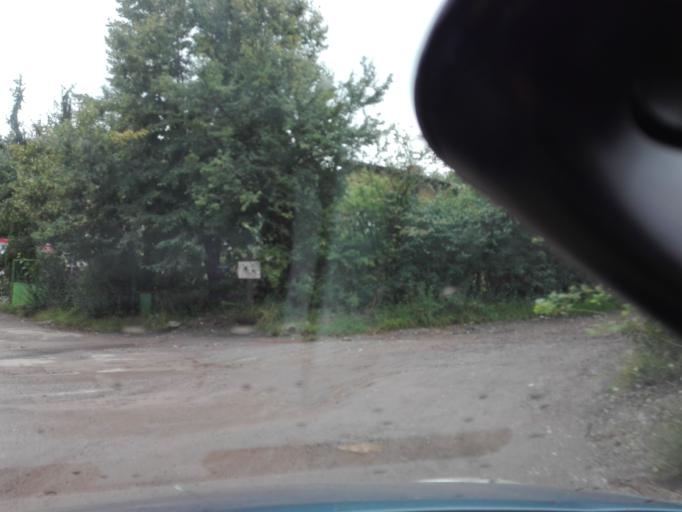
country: BG
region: Sofia-Capital
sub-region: Stolichna Obshtina
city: Sofia
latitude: 42.6029
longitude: 23.3982
